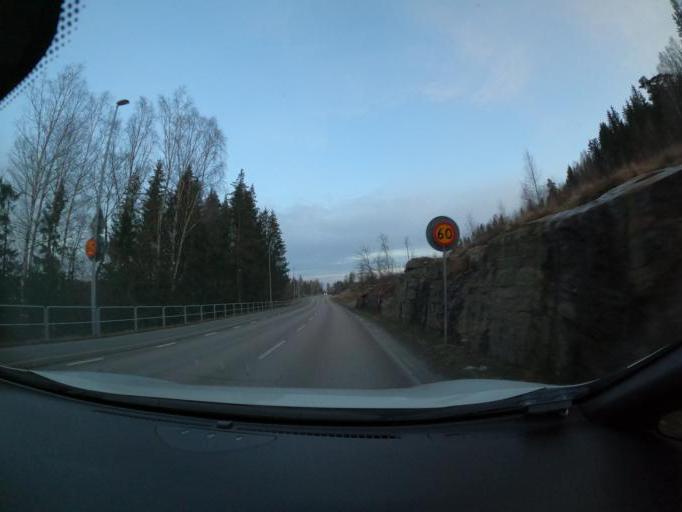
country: SE
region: Vaestra Goetaland
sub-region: Harryda Kommun
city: Molnlycke
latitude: 57.6505
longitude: 12.1554
